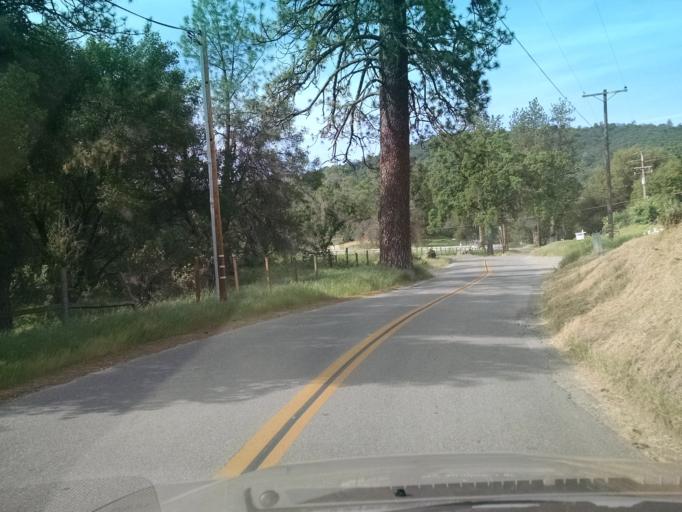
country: US
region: California
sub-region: Madera County
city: Oakhurst
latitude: 37.3155
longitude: -119.6469
